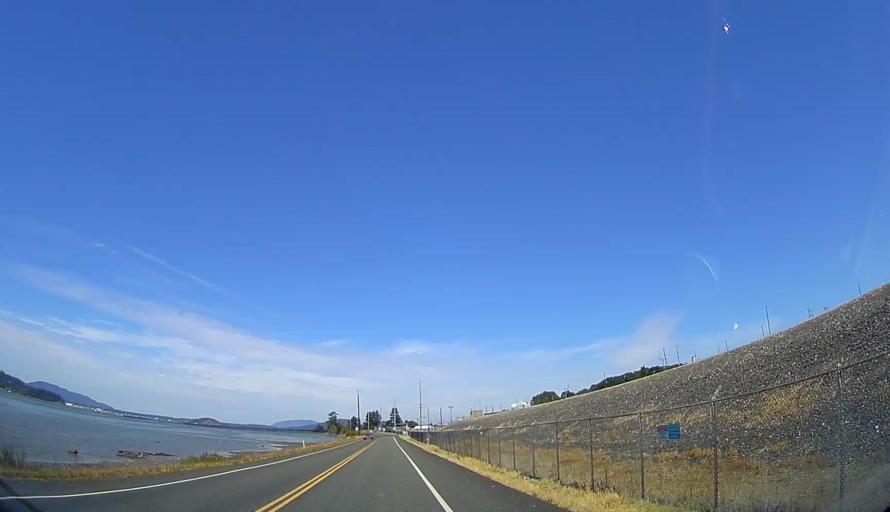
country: US
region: Washington
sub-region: Skagit County
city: Anacortes
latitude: 48.4696
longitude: -122.5708
